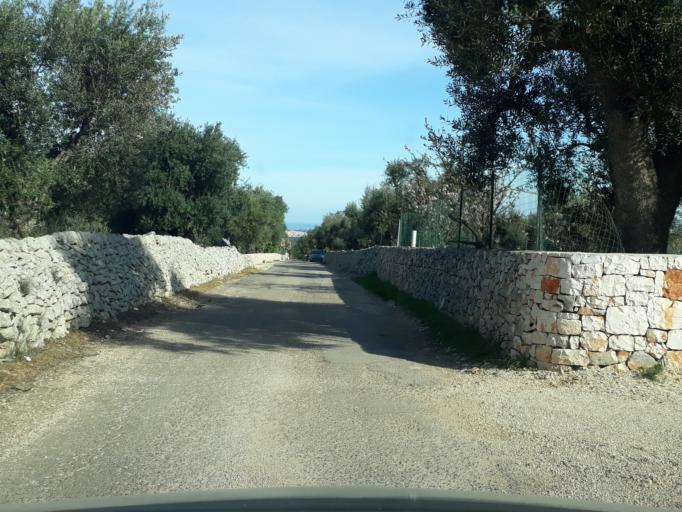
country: IT
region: Apulia
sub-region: Provincia di Brindisi
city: Lamie di Olimpie-Selva
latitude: 40.7973
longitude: 17.3692
